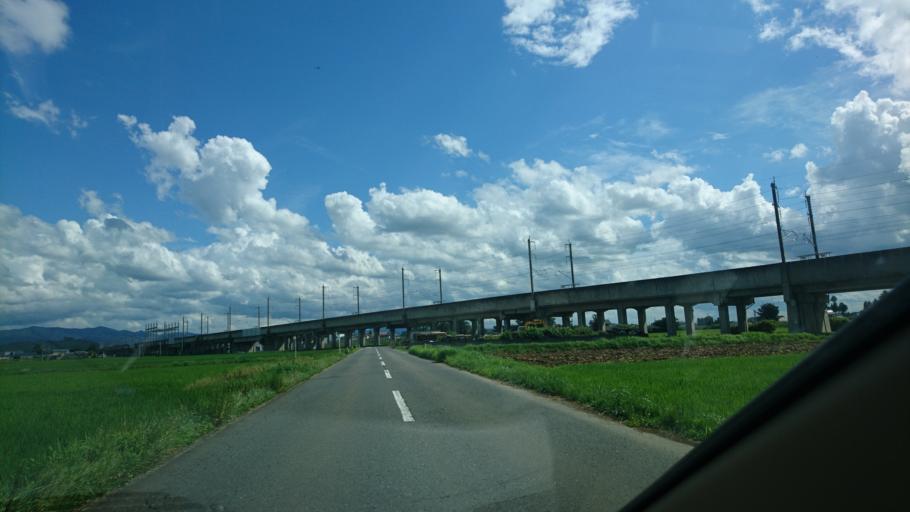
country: JP
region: Iwate
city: Mizusawa
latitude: 39.1805
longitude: 141.1723
